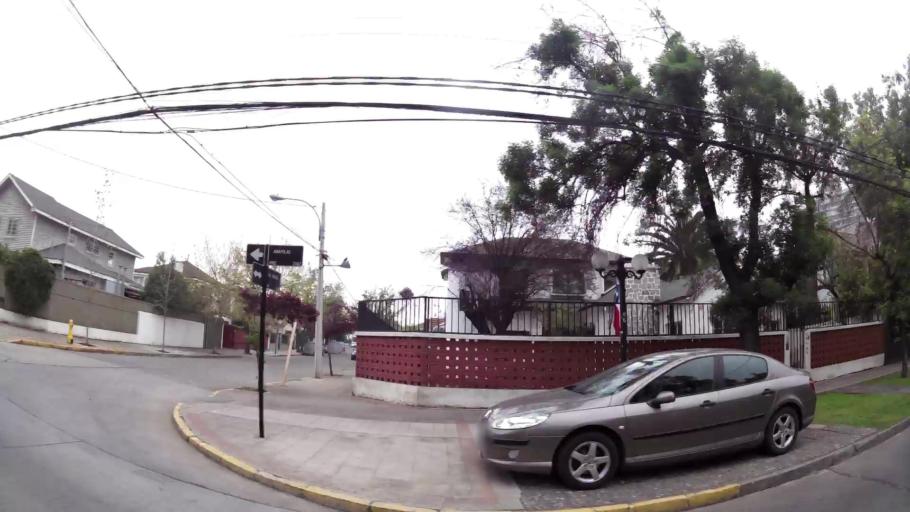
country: CL
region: Santiago Metropolitan
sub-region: Provincia de Santiago
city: Villa Presidente Frei, Nunoa, Santiago, Chile
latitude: -33.4337
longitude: -70.5892
